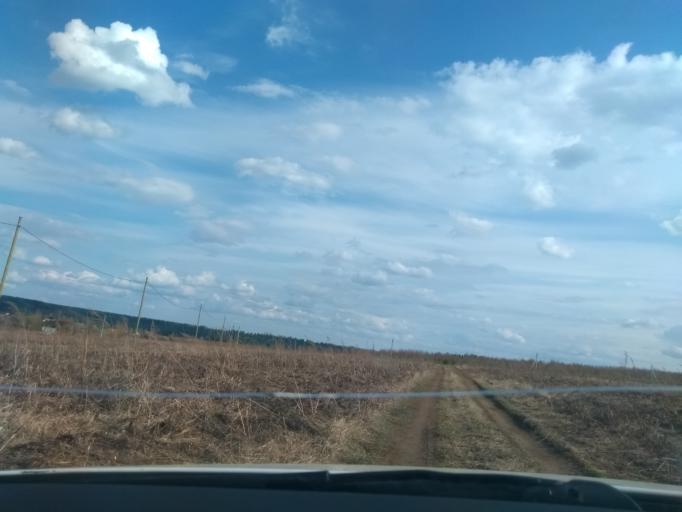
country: RU
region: Perm
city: Sylva
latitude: 57.8430
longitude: 56.7903
